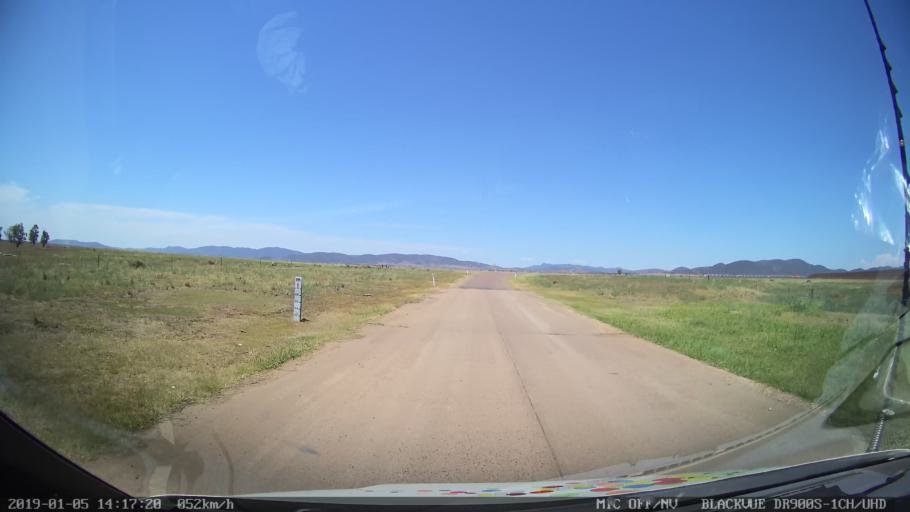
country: AU
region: New South Wales
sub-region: Liverpool Plains
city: Quirindi
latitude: -31.2548
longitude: 150.4765
